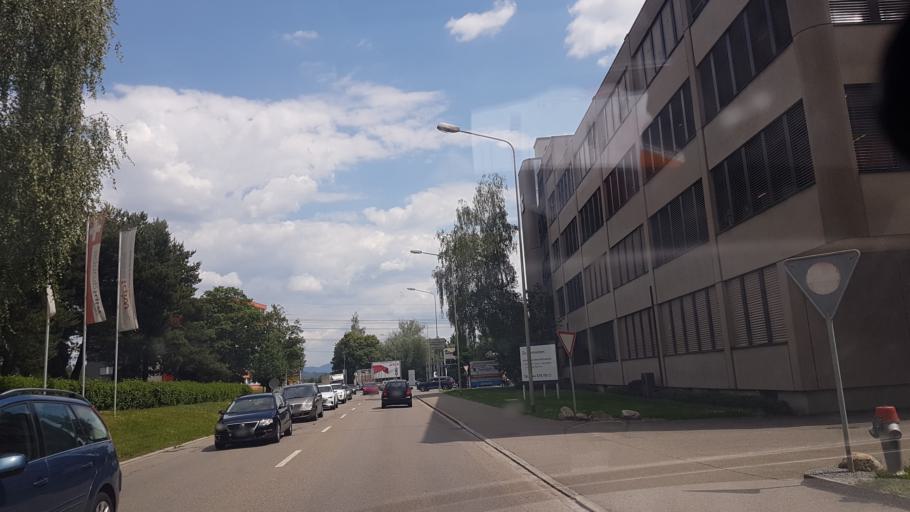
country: CH
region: Zurich
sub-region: Bezirk Uster
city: Greifensee / Muellerwis / Seilerwis
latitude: 47.3799
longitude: 8.6794
